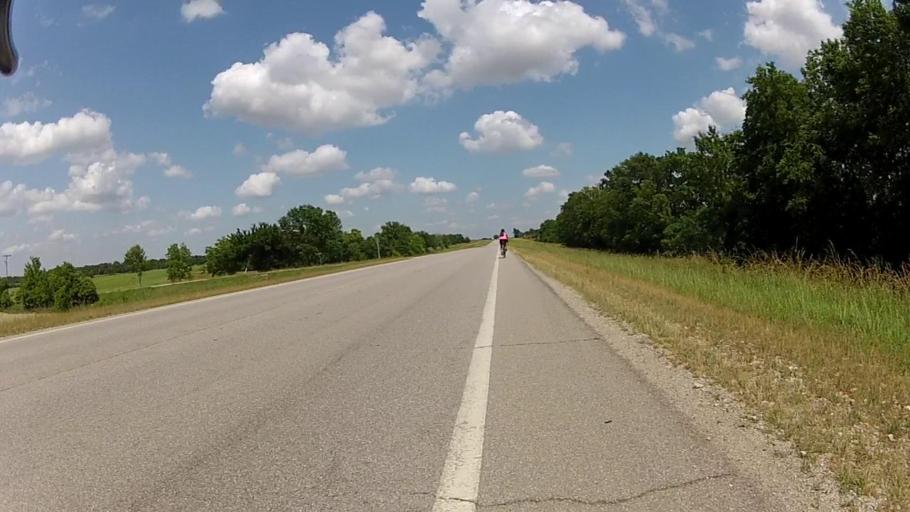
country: US
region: Kansas
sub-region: Labette County
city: Oswego
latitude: 37.1938
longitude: -95.1907
